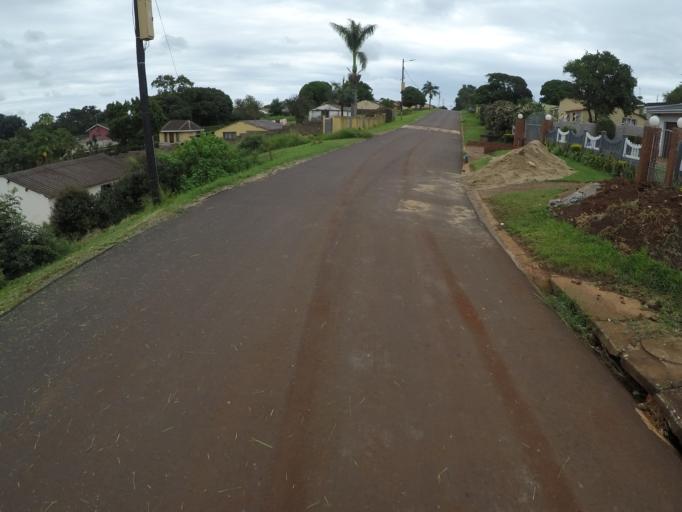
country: ZA
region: KwaZulu-Natal
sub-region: uThungulu District Municipality
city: Empangeni
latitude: -28.7688
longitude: 31.8657
